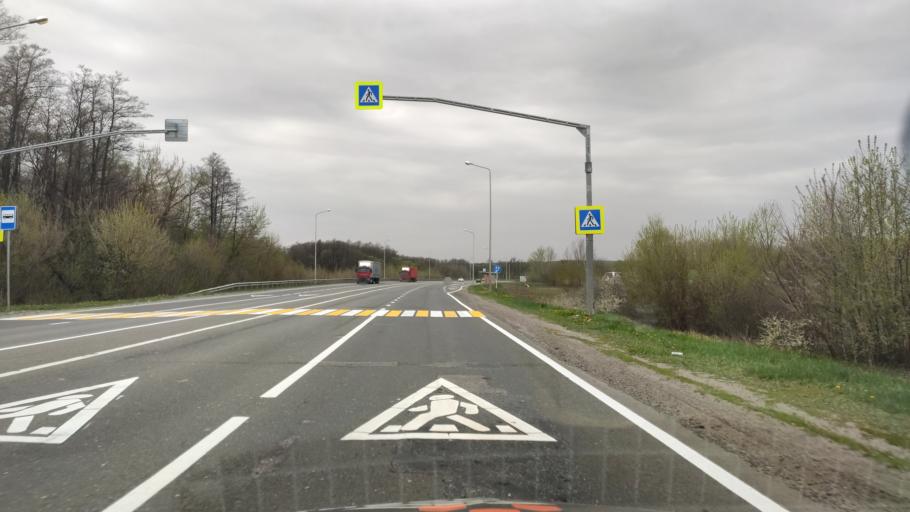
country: RU
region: Belgorod
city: Staryy Oskol
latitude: 51.3494
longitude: 37.8262
